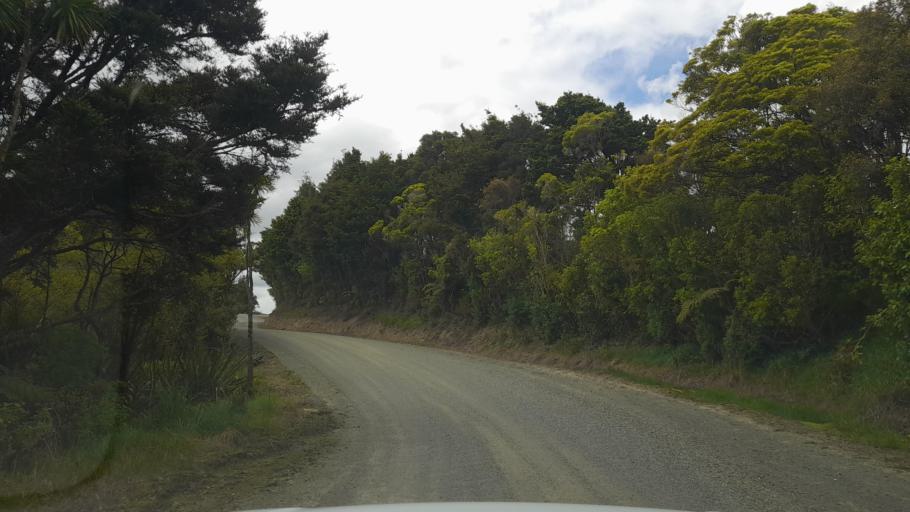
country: NZ
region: Auckland
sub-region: Auckland
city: Wellsford
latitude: -36.1813
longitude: 174.3440
